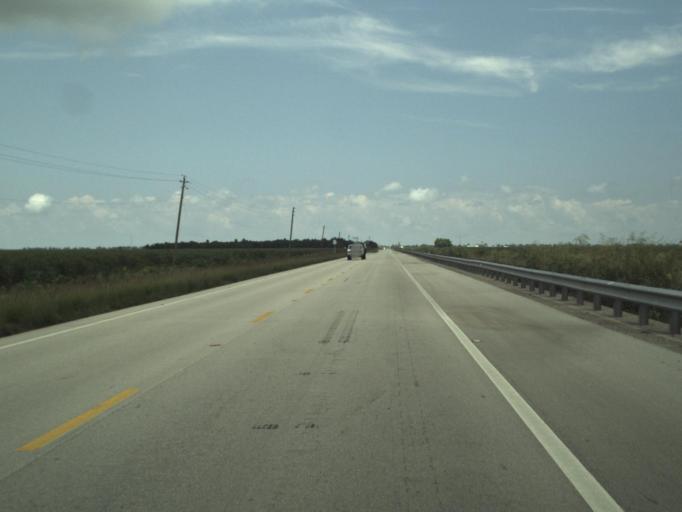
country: US
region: Florida
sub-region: Palm Beach County
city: Pahokee
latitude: 26.8302
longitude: -80.5864
